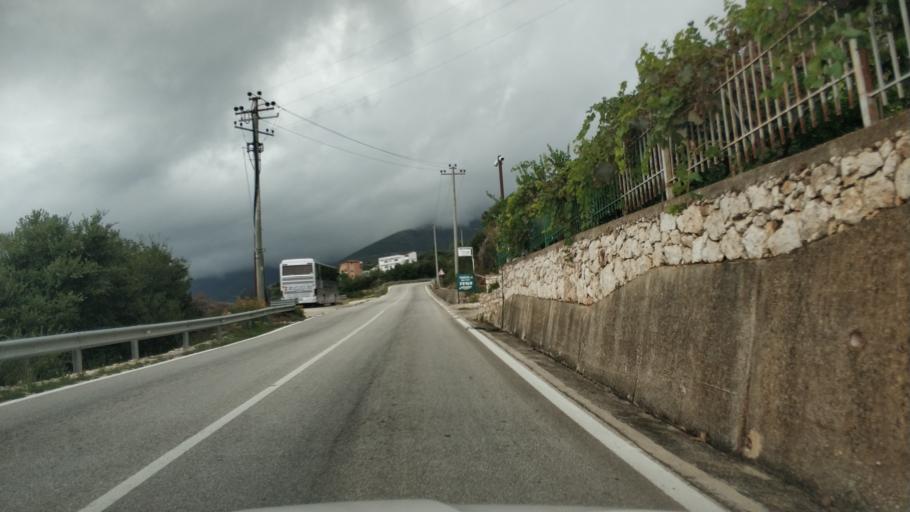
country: AL
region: Vlore
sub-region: Rrethi i Vlores
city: Vranisht
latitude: 40.1599
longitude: 19.6283
